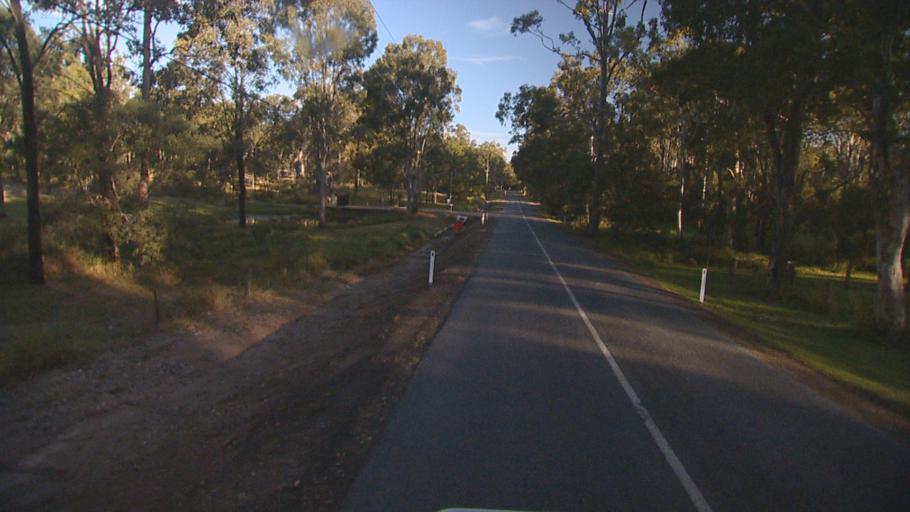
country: AU
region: Queensland
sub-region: Logan
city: Waterford West
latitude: -27.7336
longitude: 153.1457
